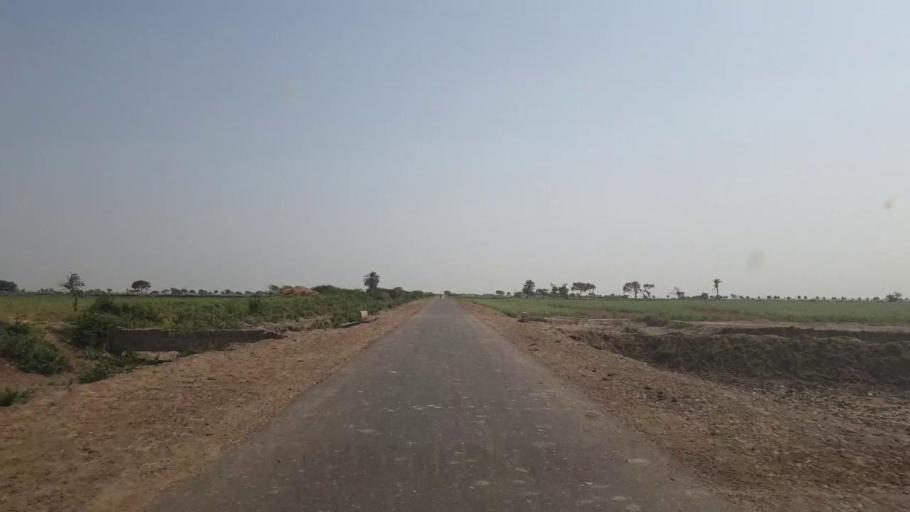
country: PK
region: Sindh
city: Jati
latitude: 24.4575
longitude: 68.5130
